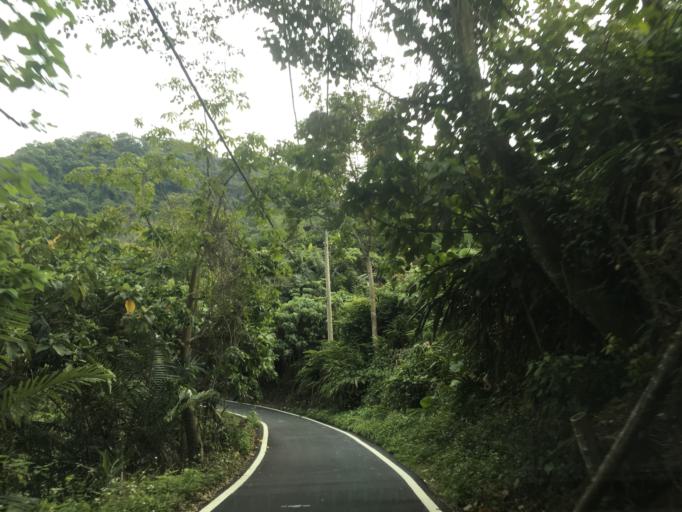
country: TW
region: Taiwan
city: Zhongxing New Village
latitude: 23.9882
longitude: 120.8122
